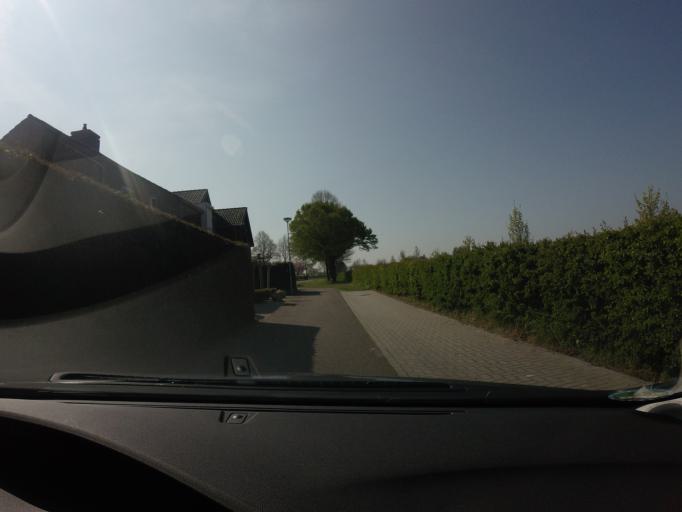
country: NL
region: Limburg
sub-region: Valkenburg aan de Geul
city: Berg
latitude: 50.8627
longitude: 5.7727
